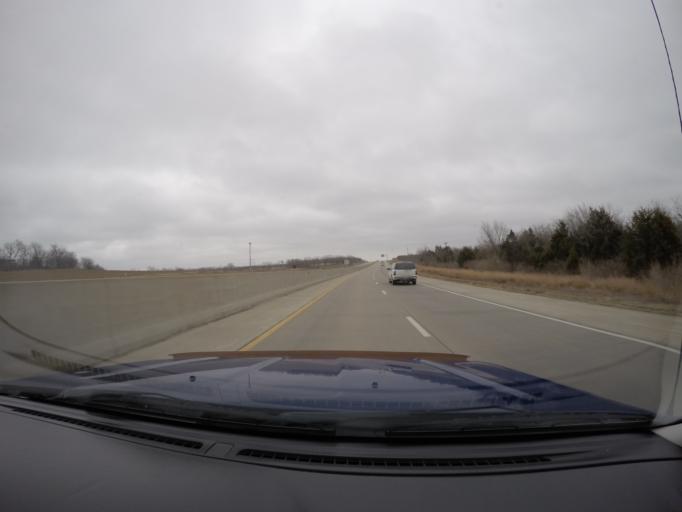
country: US
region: Kansas
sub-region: Shawnee County
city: Silver Lake
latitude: 39.0525
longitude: -95.8027
